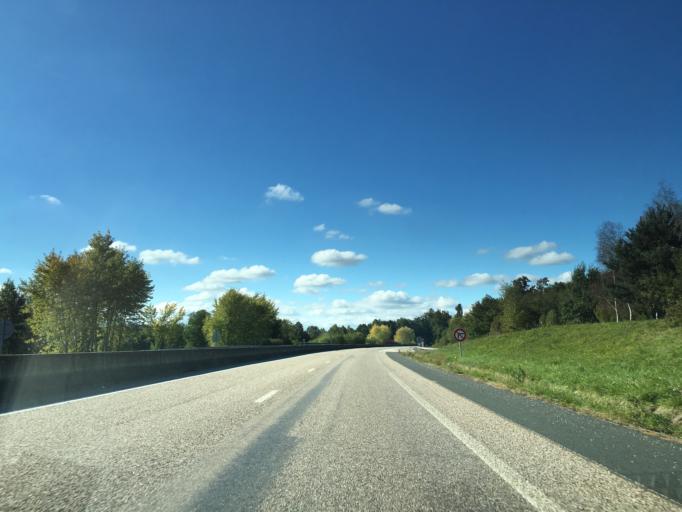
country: FR
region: Lorraine
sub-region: Departement de Meurthe-et-Moselle
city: Baccarat
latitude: 48.4381
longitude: 6.7696
